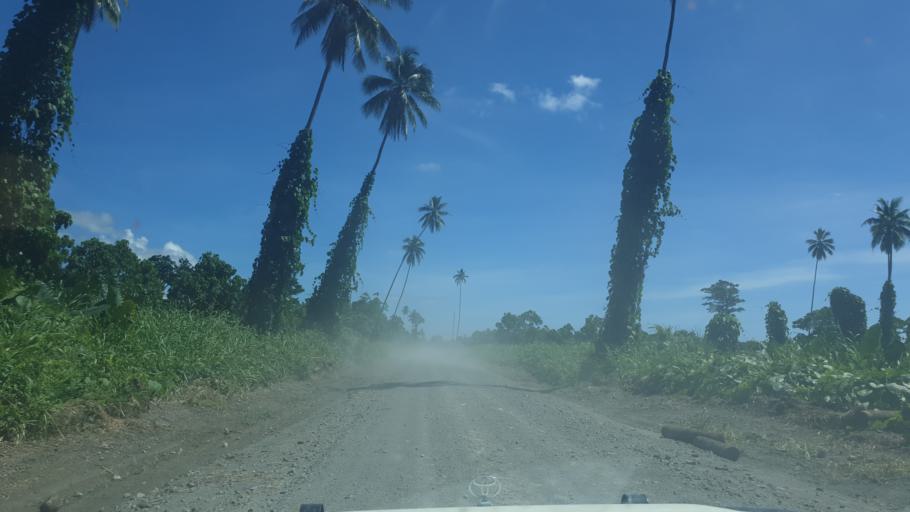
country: PG
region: Bougainville
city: Arawa
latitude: -5.9741
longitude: 155.3477
